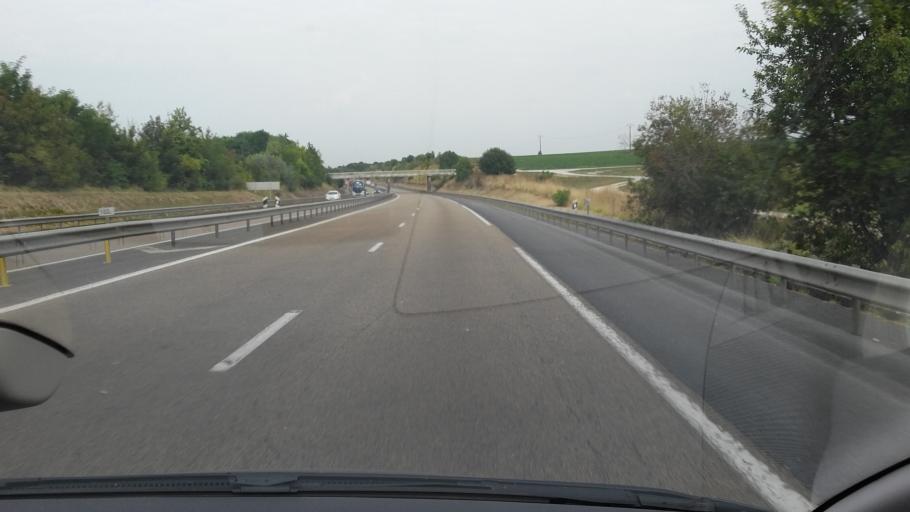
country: FR
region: Champagne-Ardenne
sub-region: Departement de la Marne
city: Witry-les-Reims
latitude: 49.2847
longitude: 4.1182
